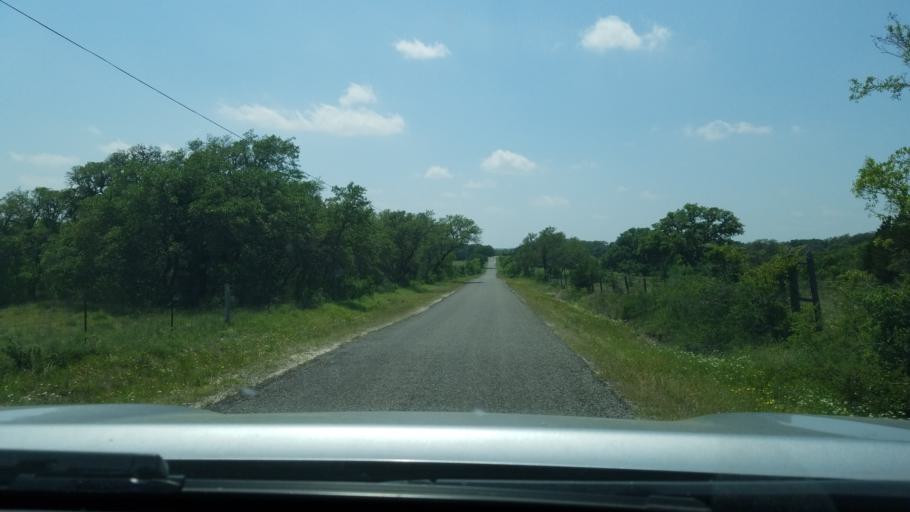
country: US
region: Texas
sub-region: Blanco County
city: Blanco
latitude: 29.9912
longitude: -98.5266
